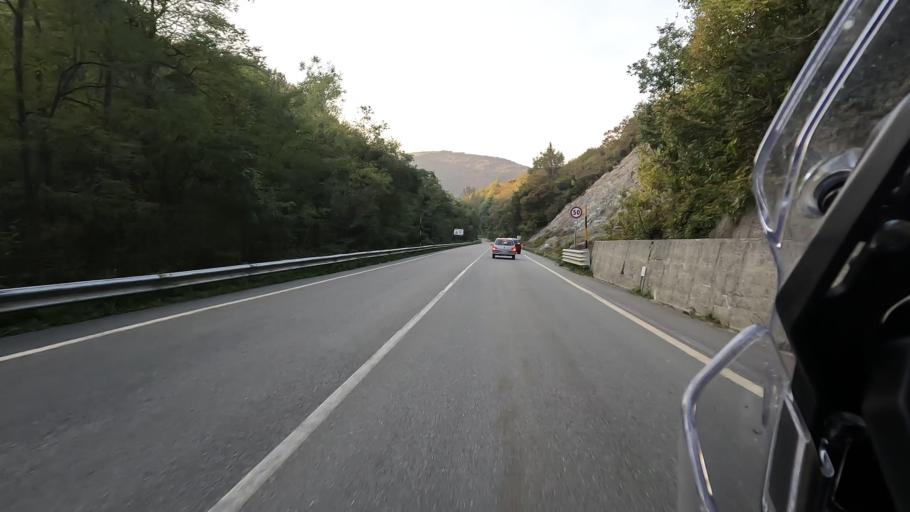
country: IT
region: Liguria
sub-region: Provincia di Savona
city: Osteria dei Cacciatori-Stella
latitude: 44.4441
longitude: 8.4838
